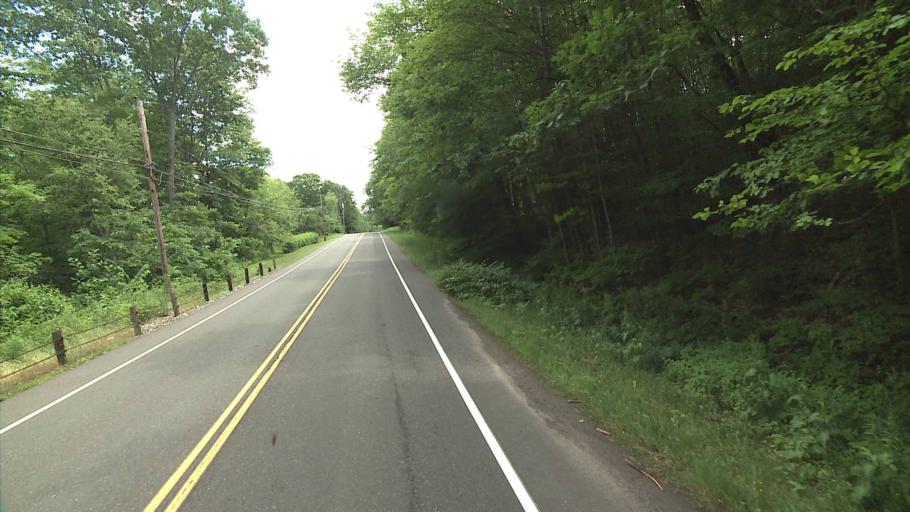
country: US
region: Connecticut
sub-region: Litchfield County
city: Bethlehem Village
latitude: 41.6706
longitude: -73.1691
